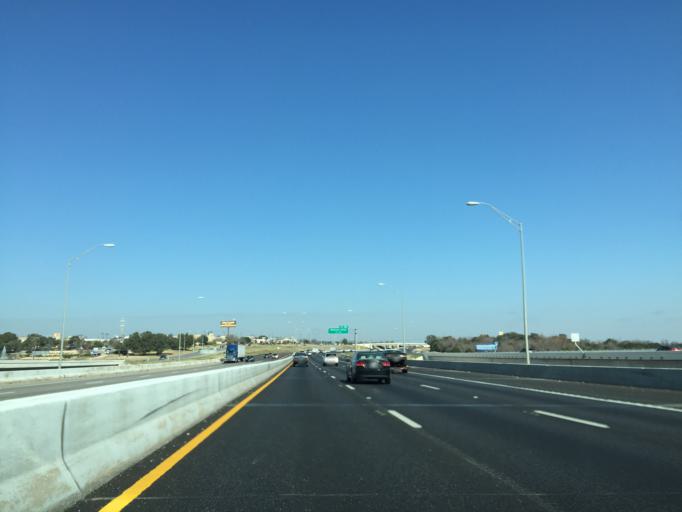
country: US
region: Texas
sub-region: Williamson County
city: Georgetown
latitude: 30.6253
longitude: -97.6908
